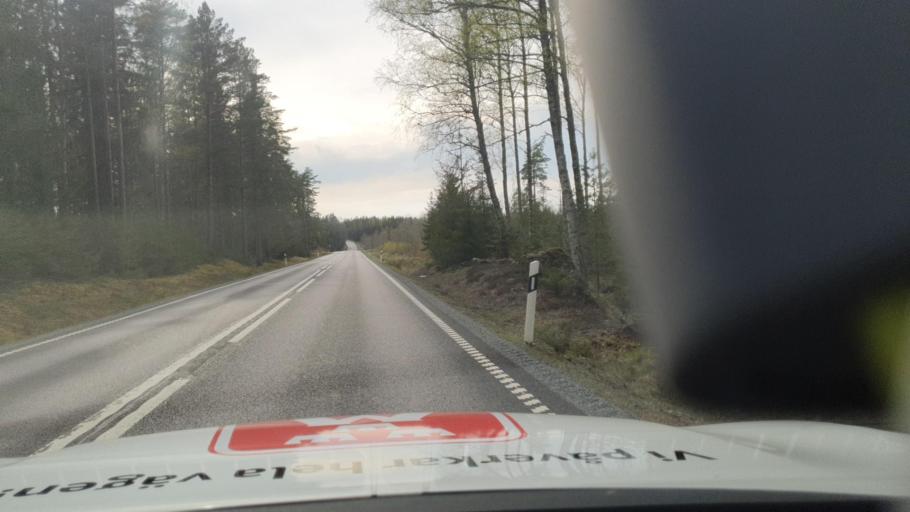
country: SE
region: Soedermanland
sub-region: Flens Kommun
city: Malmkoping
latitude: 59.2173
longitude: 16.8889
